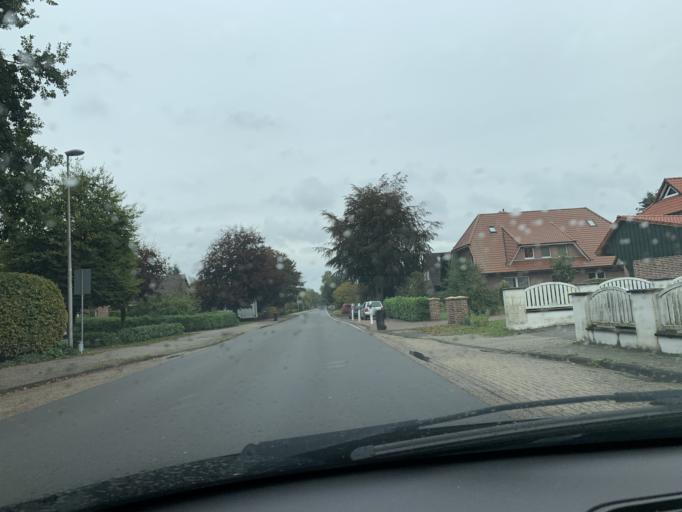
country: DE
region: Lower Saxony
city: Bad Zwischenahn
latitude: 53.1505
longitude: 8.0842
